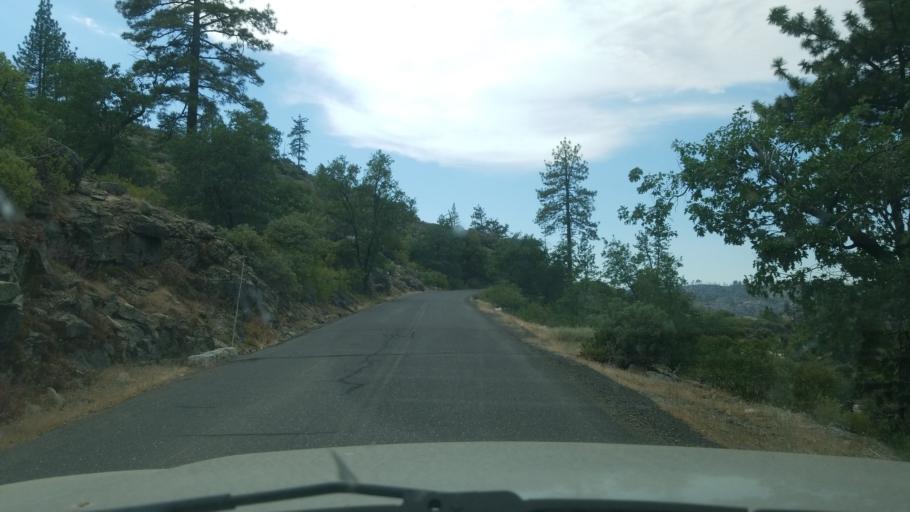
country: US
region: California
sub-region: Mariposa County
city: Yosemite Valley
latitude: 37.9025
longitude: -119.8198
